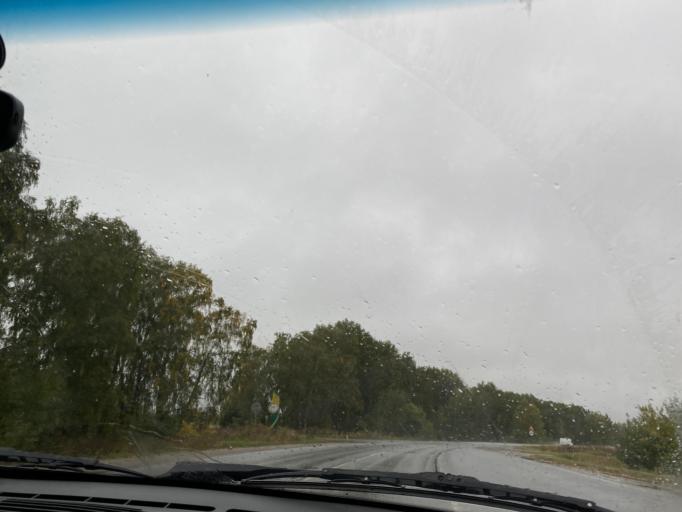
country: RU
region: Rjazan
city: Murmino
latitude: 54.4625
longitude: 39.8695
